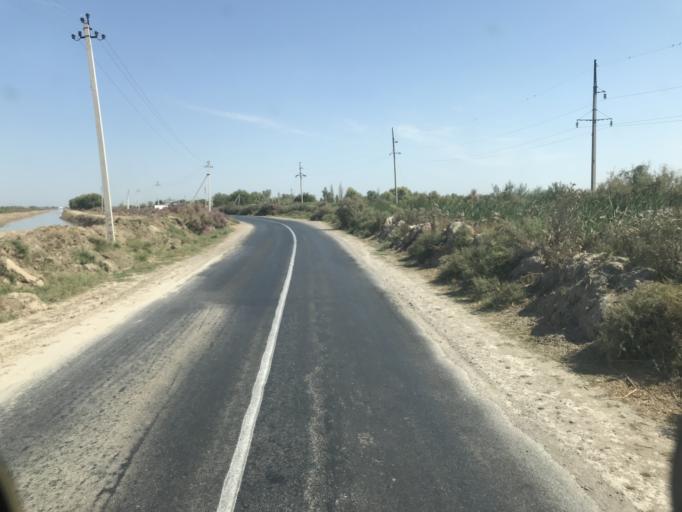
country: KZ
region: Ongtustik Qazaqstan
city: Myrzakent
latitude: 40.7274
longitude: 68.5360
